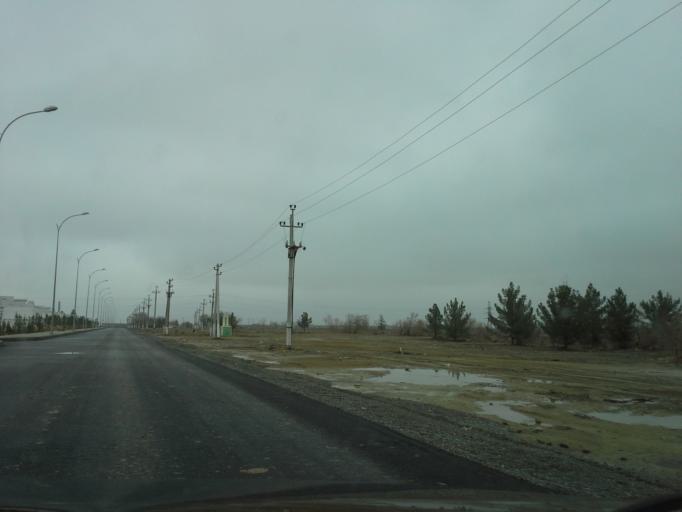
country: TM
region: Ahal
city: Ashgabat
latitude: 37.9702
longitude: 58.4070
